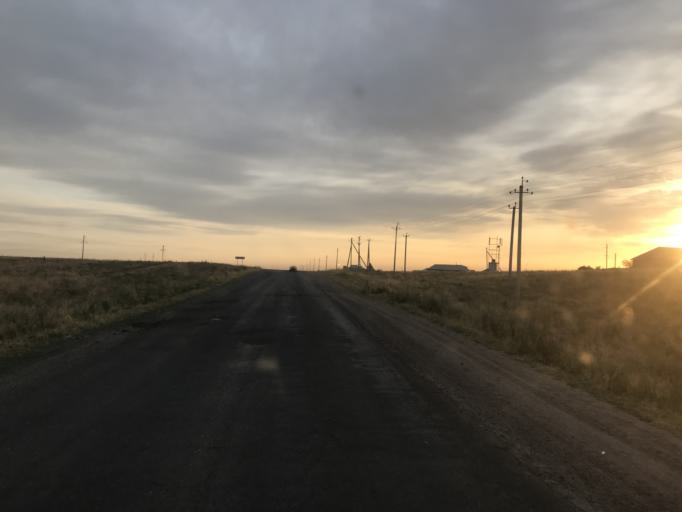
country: UZ
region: Toshkent
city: Amir Timur
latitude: 41.2359
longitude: 68.8119
